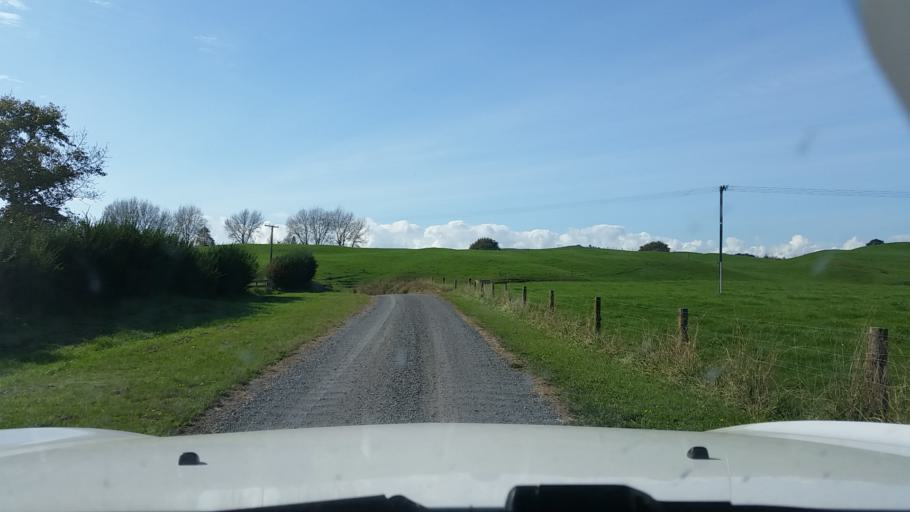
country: NZ
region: Waikato
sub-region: Matamata-Piako District
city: Matamata
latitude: -37.7269
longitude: 175.6341
